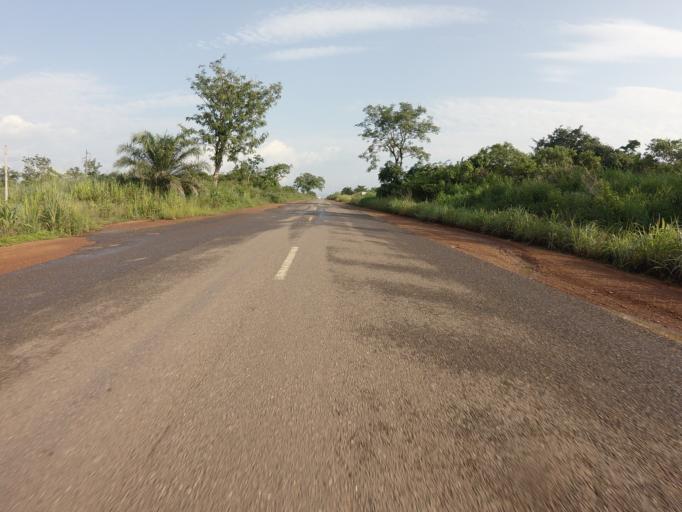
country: GH
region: Volta
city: Hohoe
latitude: 7.0307
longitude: 0.4274
